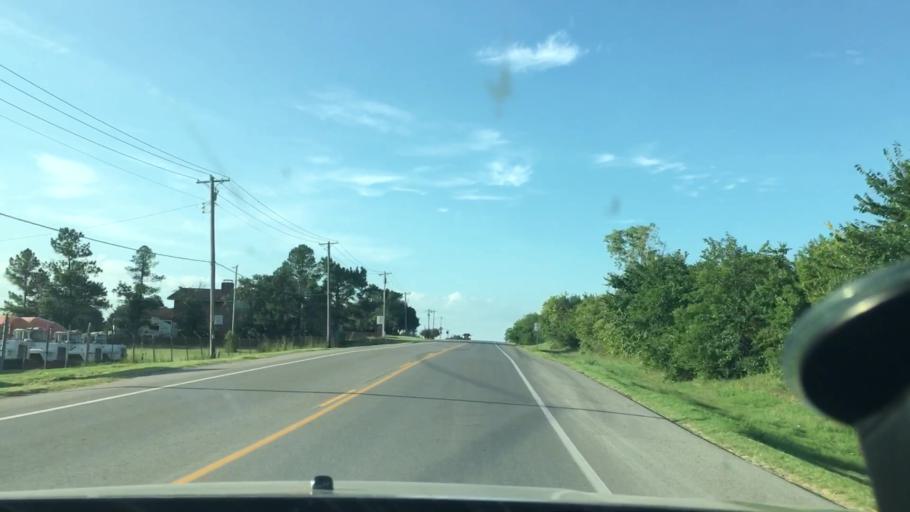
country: US
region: Oklahoma
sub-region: Garvin County
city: Pauls Valley
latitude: 34.7181
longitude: -97.2130
